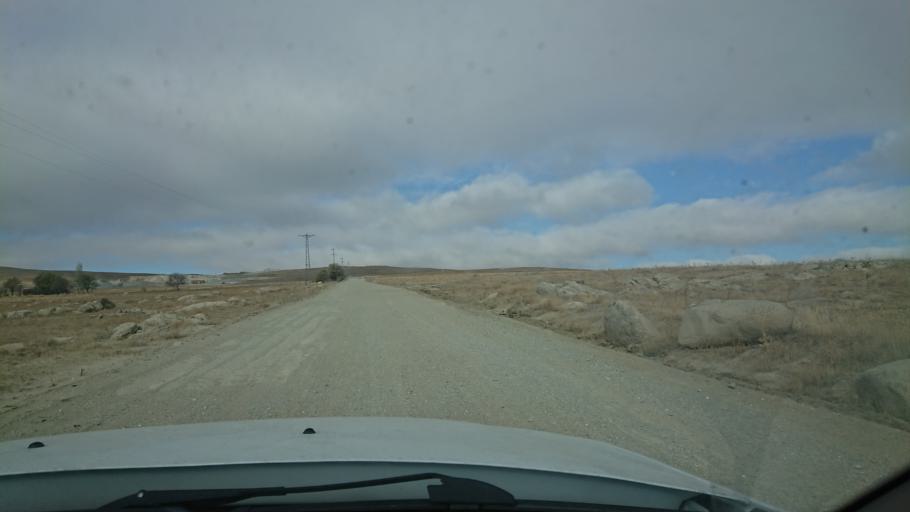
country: TR
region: Aksaray
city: Ortakoy
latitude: 38.7713
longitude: 34.0152
